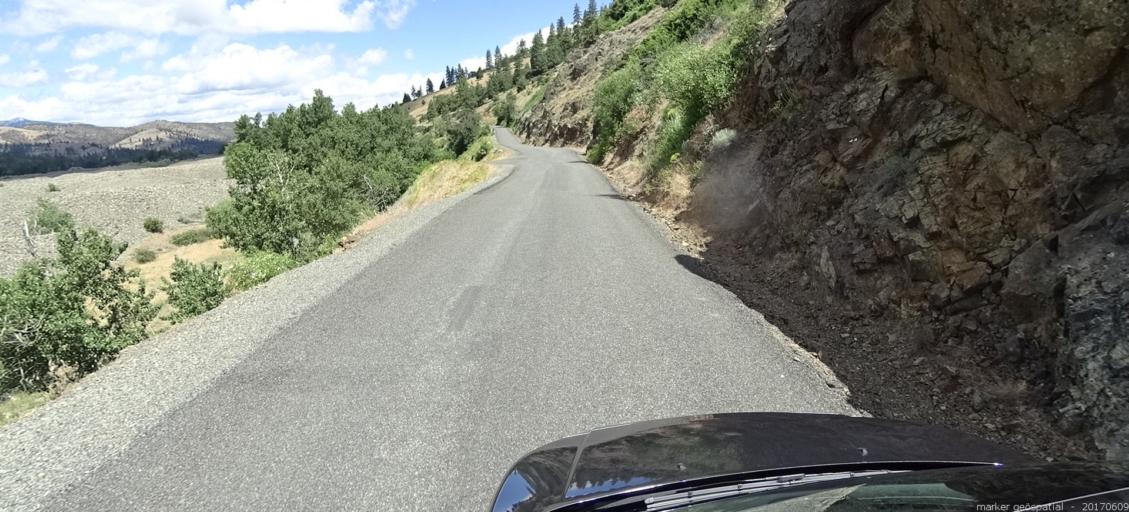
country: US
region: California
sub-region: Siskiyou County
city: Weed
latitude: 41.3231
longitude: -122.8089
